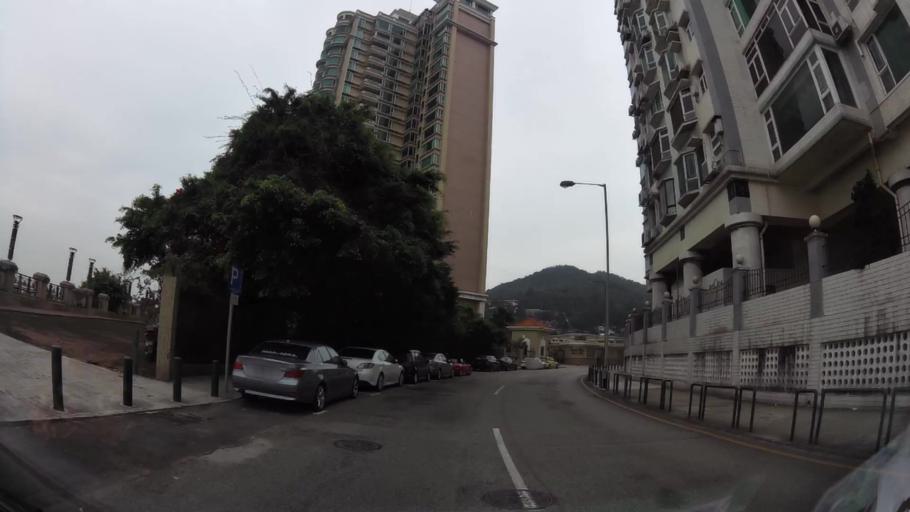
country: MO
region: Macau
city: Macau
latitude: 22.1652
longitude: 113.5605
